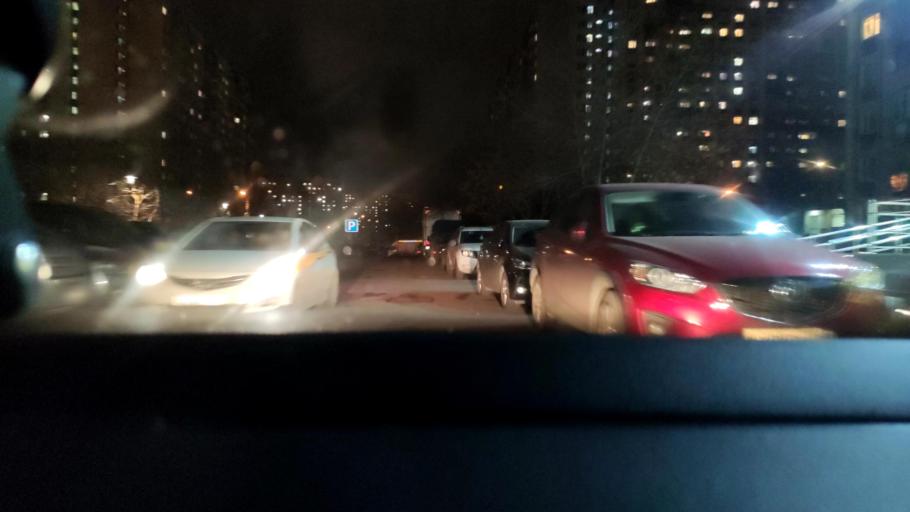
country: RU
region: Moskovskaya
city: Pavshino
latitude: 55.8518
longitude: 37.3473
